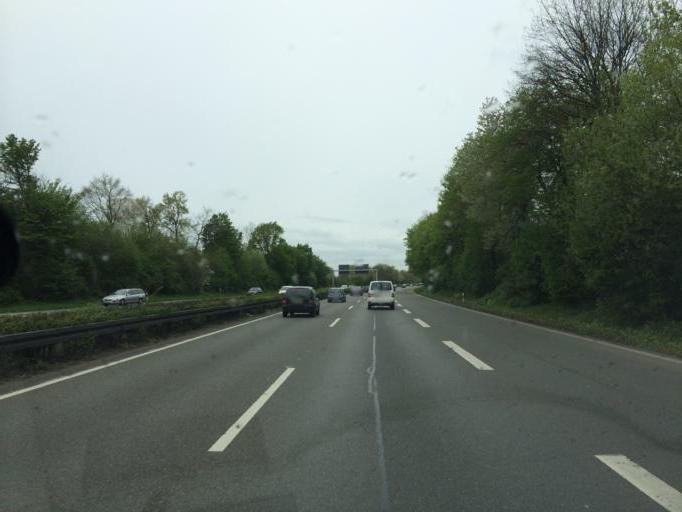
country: DE
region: North Rhine-Westphalia
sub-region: Regierungsbezirk Arnsberg
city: Herne
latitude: 51.5465
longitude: 7.1987
